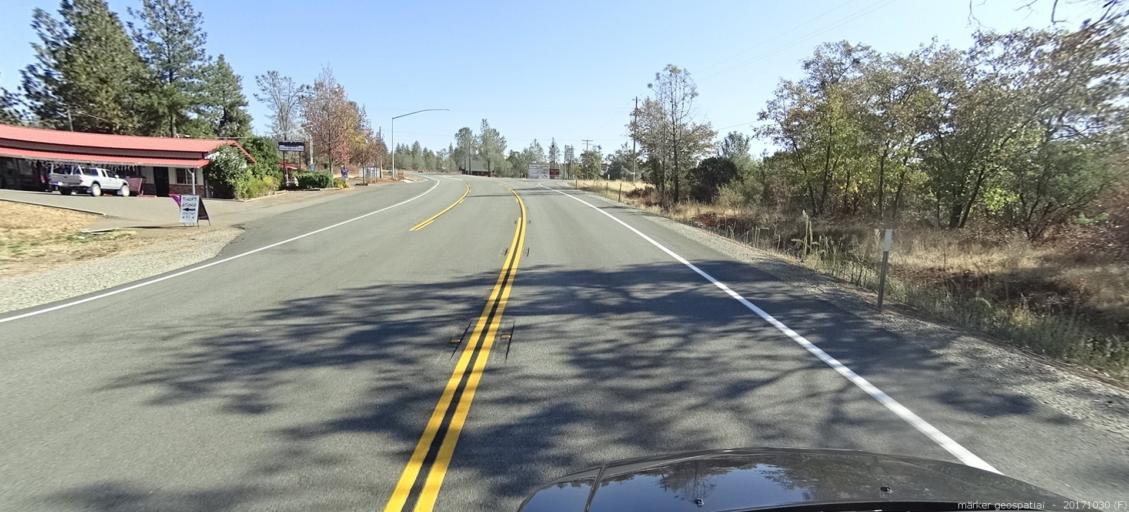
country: US
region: California
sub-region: Shasta County
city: Shingletown
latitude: 40.5018
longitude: -121.9956
